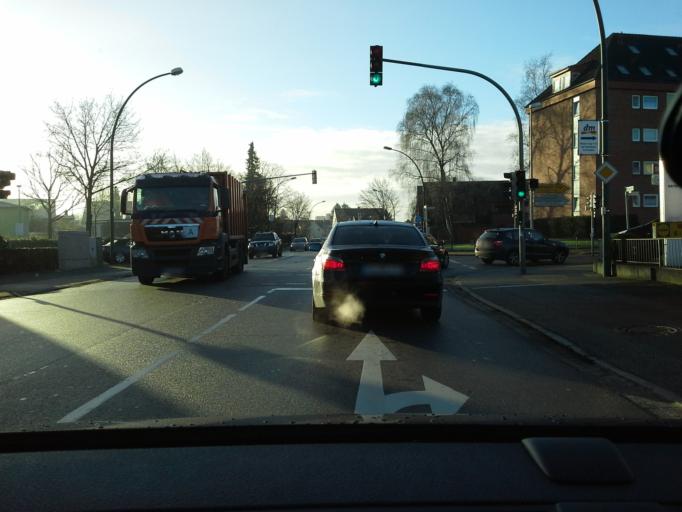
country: DE
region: Schleswig-Holstein
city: Pinneberg
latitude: 53.6703
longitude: 9.7940
